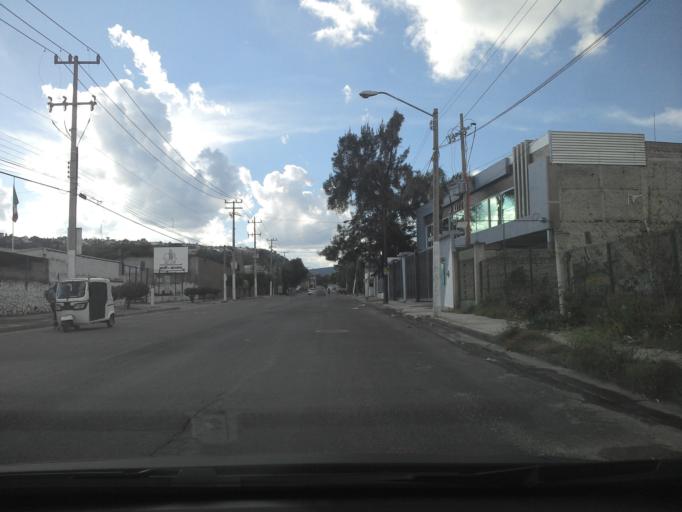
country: MX
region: Jalisco
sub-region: Tlajomulco de Zuniga
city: Palomar
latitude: 20.6173
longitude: -103.4490
